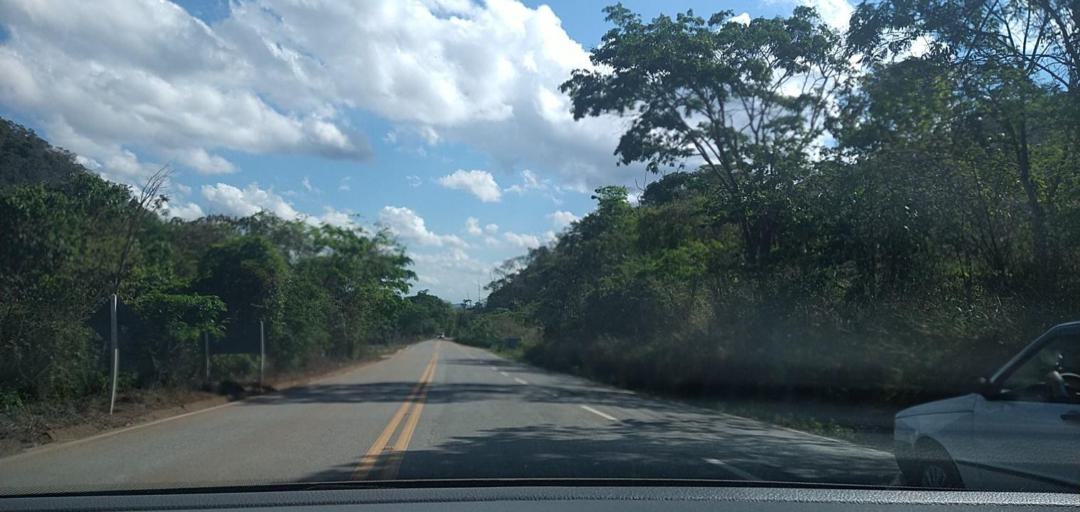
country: BR
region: Minas Gerais
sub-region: Alvinopolis
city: Alvinopolis
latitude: -20.0423
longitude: -43.0319
